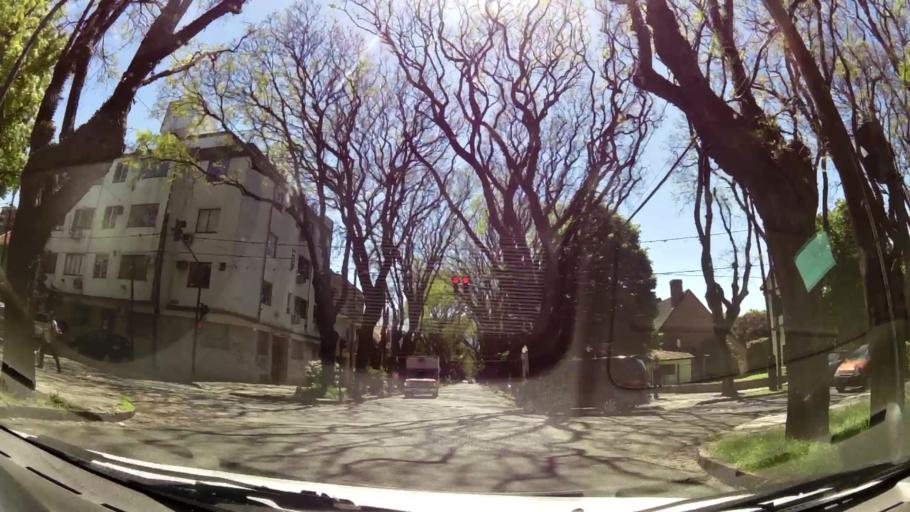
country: AR
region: Buenos Aires
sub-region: Partido de Vicente Lopez
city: Olivos
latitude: -34.5107
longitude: -58.4844
